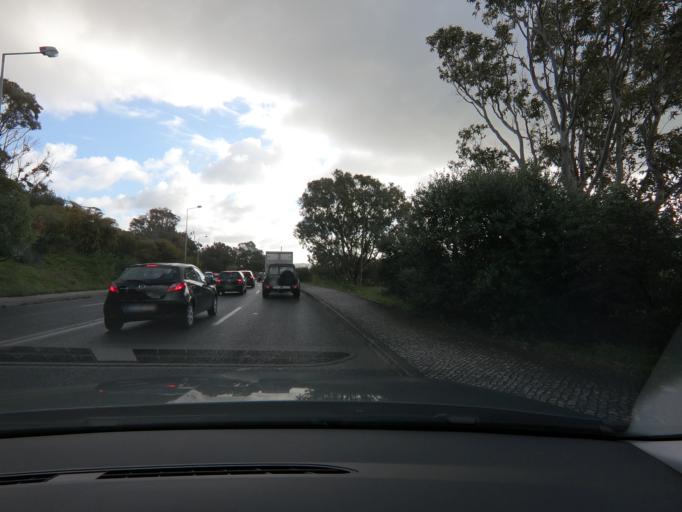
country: PT
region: Lisbon
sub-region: Oeiras
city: Oeiras
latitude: 38.6866
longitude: -9.3038
